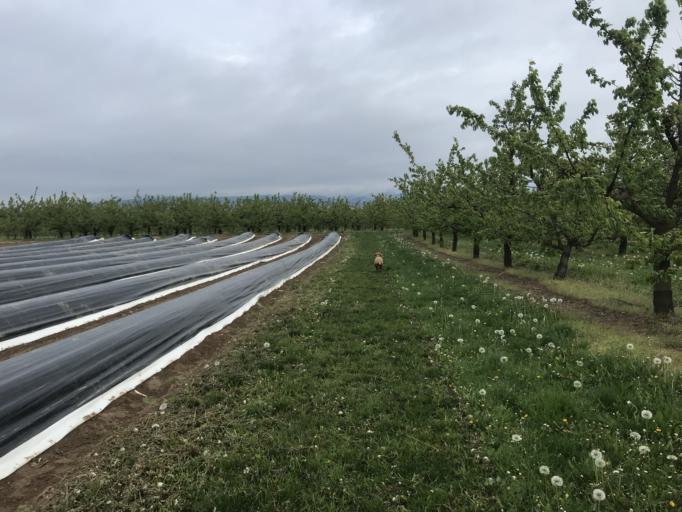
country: DE
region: Rheinland-Pfalz
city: Budenheim
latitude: 49.9748
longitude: 8.1627
